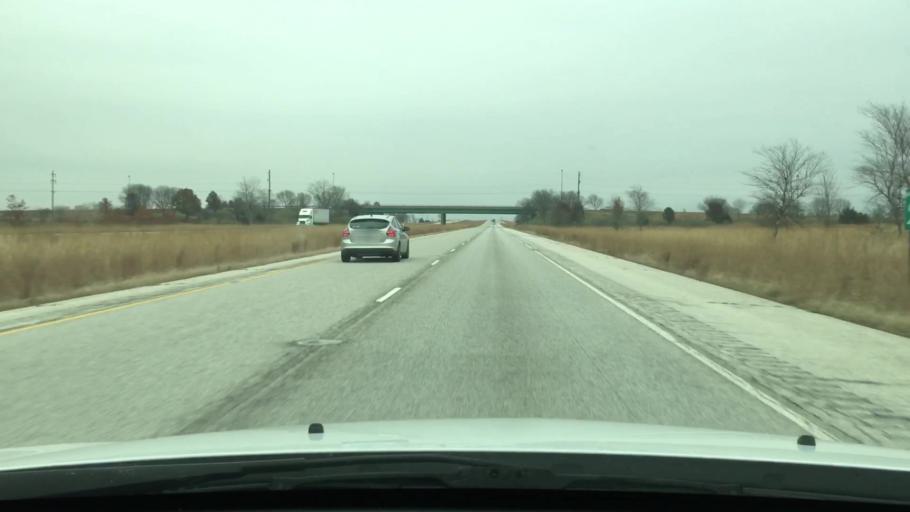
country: US
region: Illinois
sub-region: Morgan County
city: South Jacksonville
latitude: 39.6864
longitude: -90.2324
